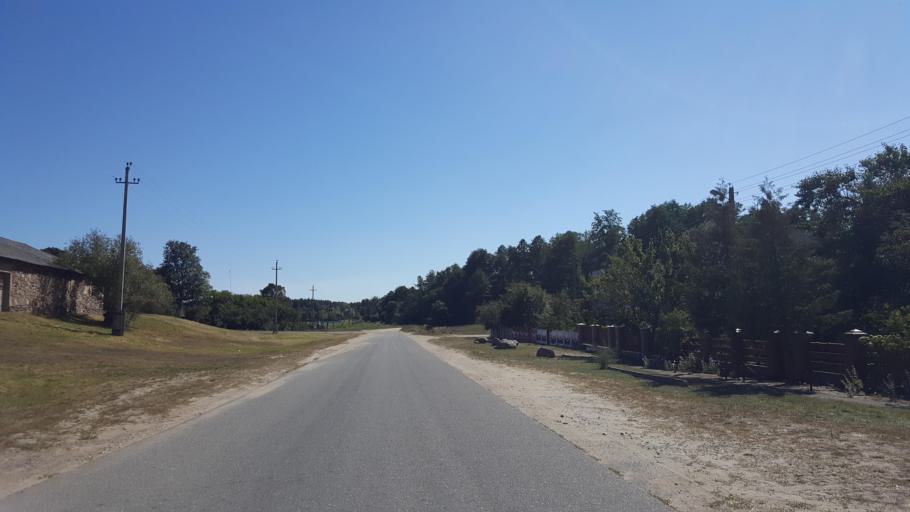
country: PL
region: Lublin Voivodeship
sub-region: Powiat bialski
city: Rokitno
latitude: 52.2271
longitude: 23.3448
